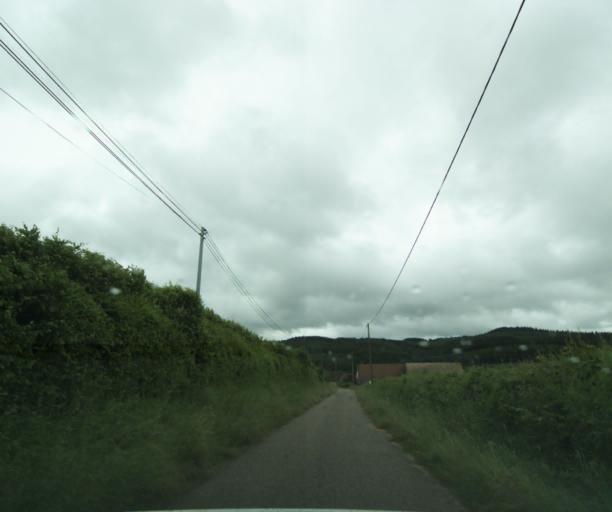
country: FR
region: Bourgogne
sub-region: Departement de Saone-et-Loire
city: Matour
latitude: 46.4555
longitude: 4.4587
